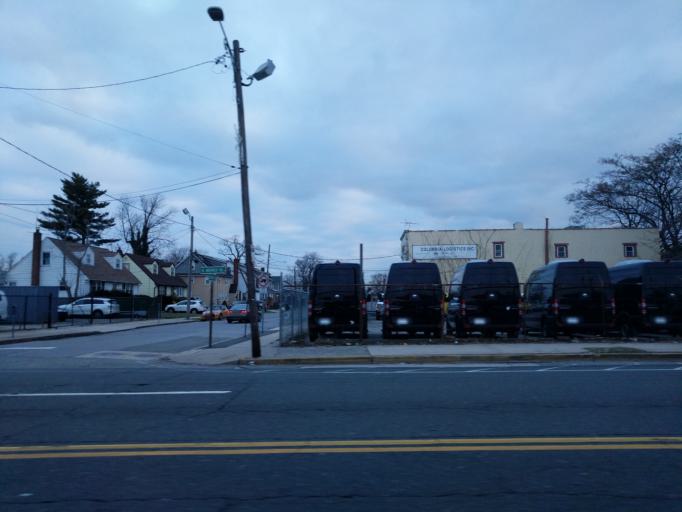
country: US
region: New York
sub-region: Nassau County
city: Valley Stream
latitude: 40.6687
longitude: -73.7133
